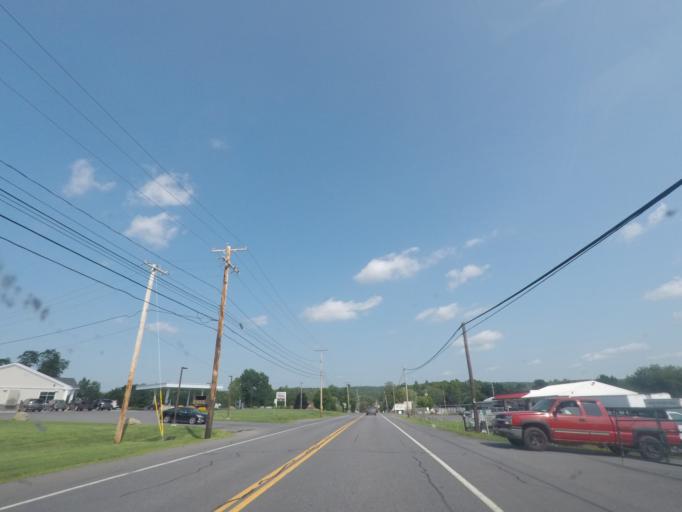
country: US
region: New York
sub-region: Rensselaer County
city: Nassau
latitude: 42.5178
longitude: -73.6192
